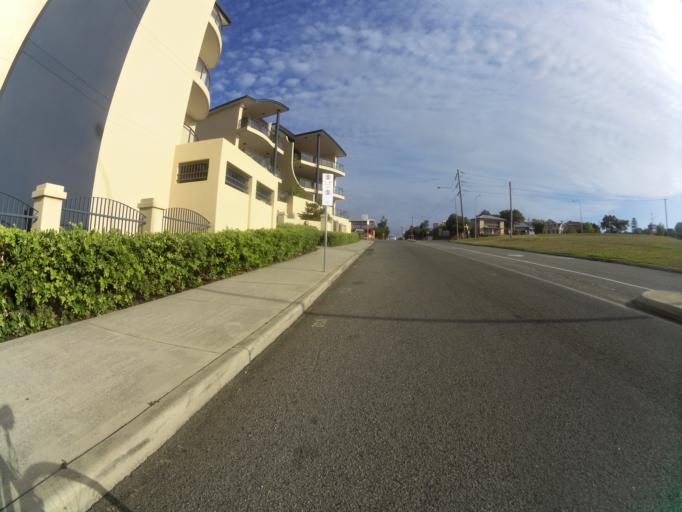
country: AU
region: Western Australia
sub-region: East Fremantle
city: East Fremantle
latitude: -32.0415
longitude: 115.7581
